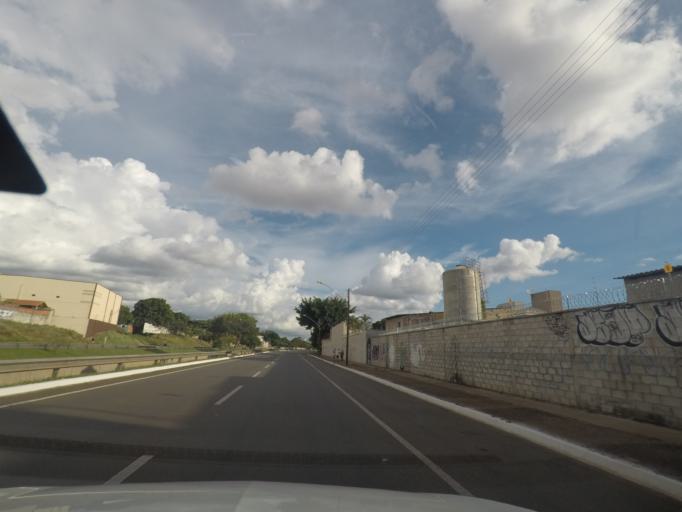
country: BR
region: Goias
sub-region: Goiania
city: Goiania
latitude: -16.6778
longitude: -49.2943
